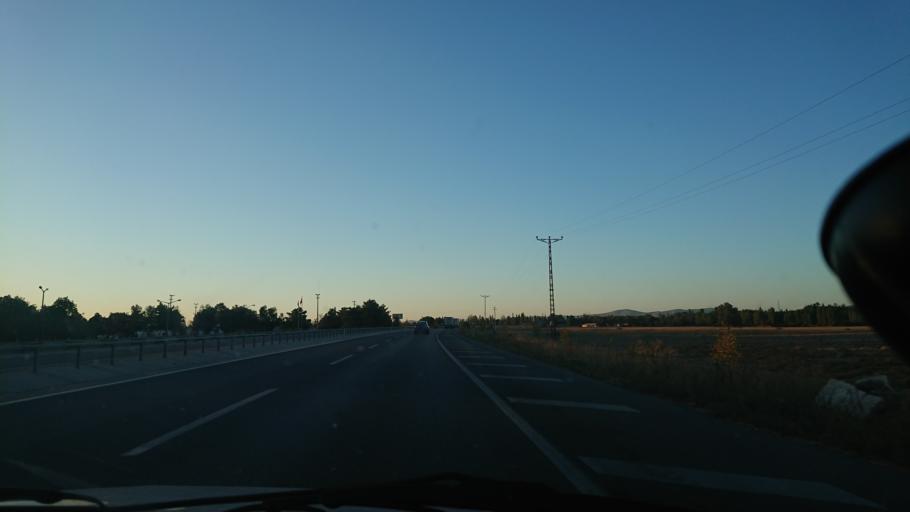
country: TR
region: Eskisehir
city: Mahmudiye
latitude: 39.5599
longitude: 30.9173
